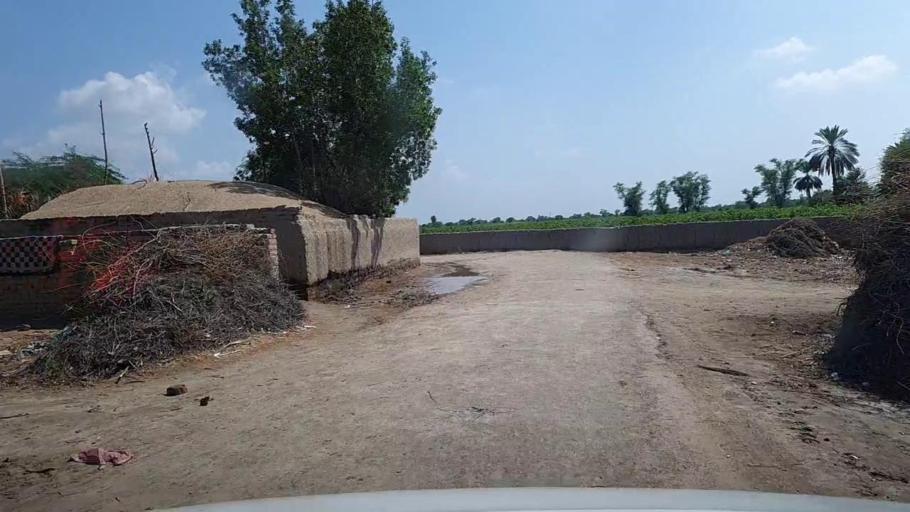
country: PK
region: Sindh
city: Kandiaro
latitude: 27.0035
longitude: 68.3059
